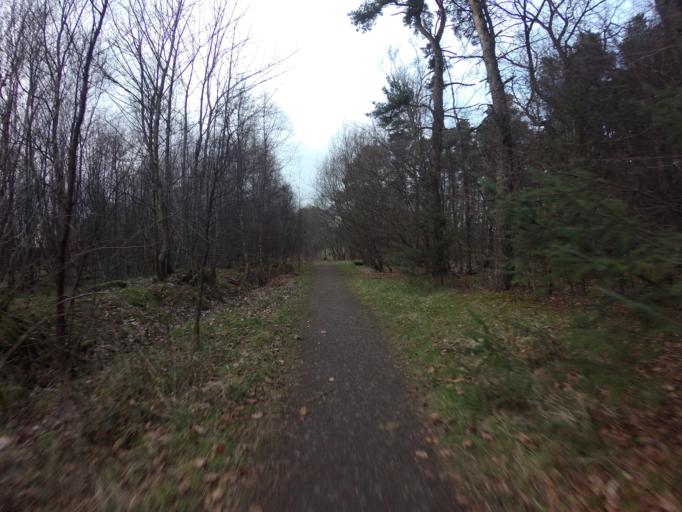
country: GB
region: Scotland
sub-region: West Lothian
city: Livingston
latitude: 55.8935
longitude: -3.5534
